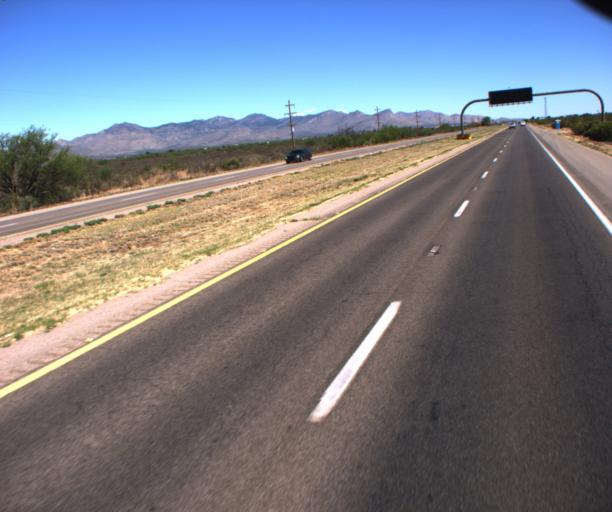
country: US
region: Arizona
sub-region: Cochise County
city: Huachuca City
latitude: 31.6692
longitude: -110.3502
